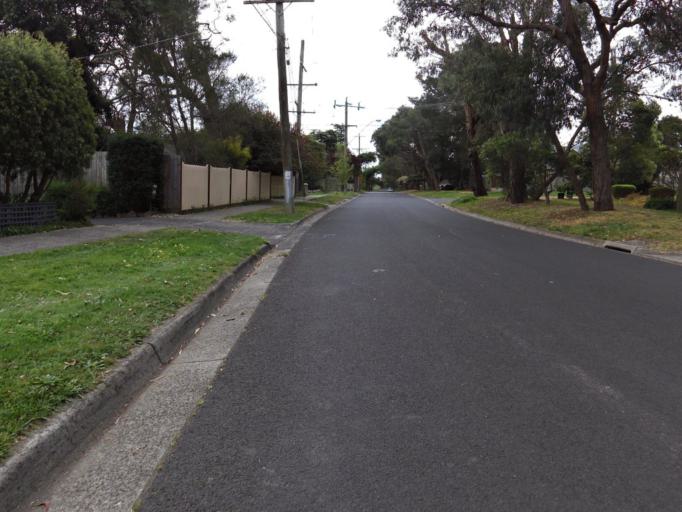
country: AU
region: Victoria
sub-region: Maroondah
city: Heathmont
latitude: -37.8346
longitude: 145.2303
